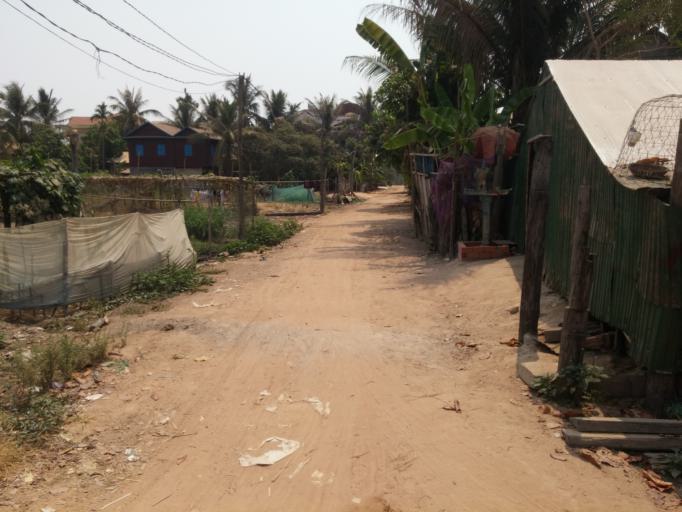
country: KH
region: Siem Reap
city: Siem Reap
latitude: 13.3606
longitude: 103.8923
